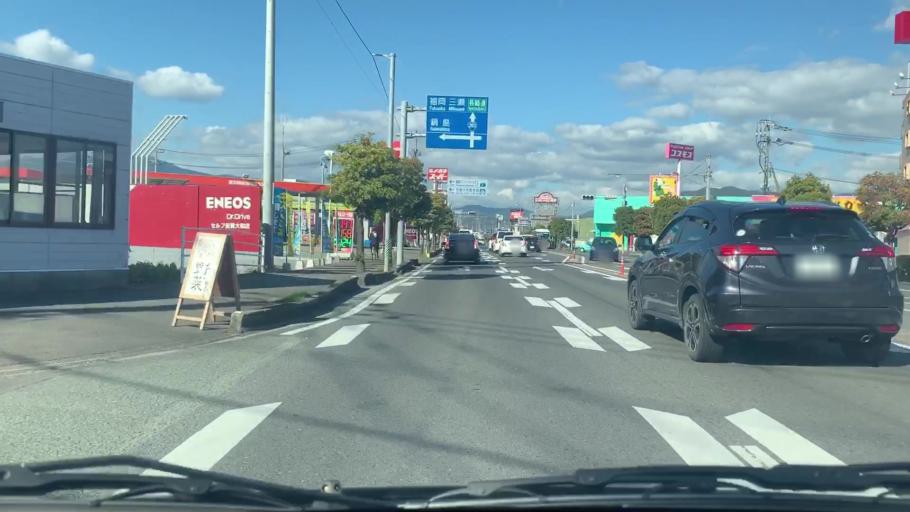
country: JP
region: Saga Prefecture
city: Saga-shi
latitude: 33.2909
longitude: 130.2865
